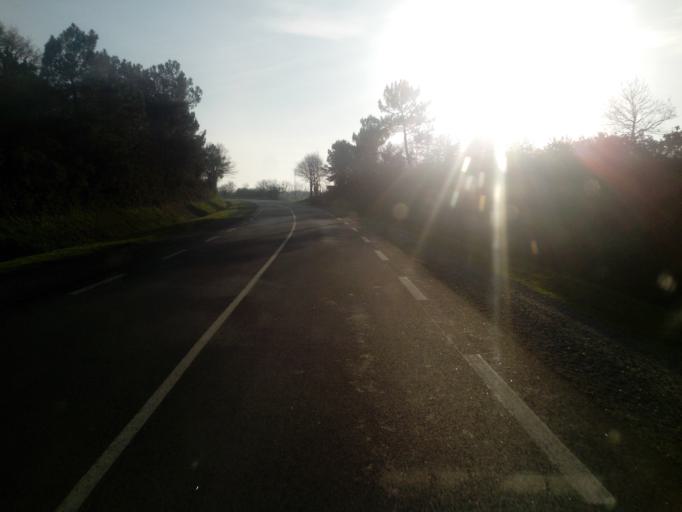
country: FR
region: Brittany
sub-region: Departement du Morbihan
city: Mauron
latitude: 48.0440
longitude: -2.3034
